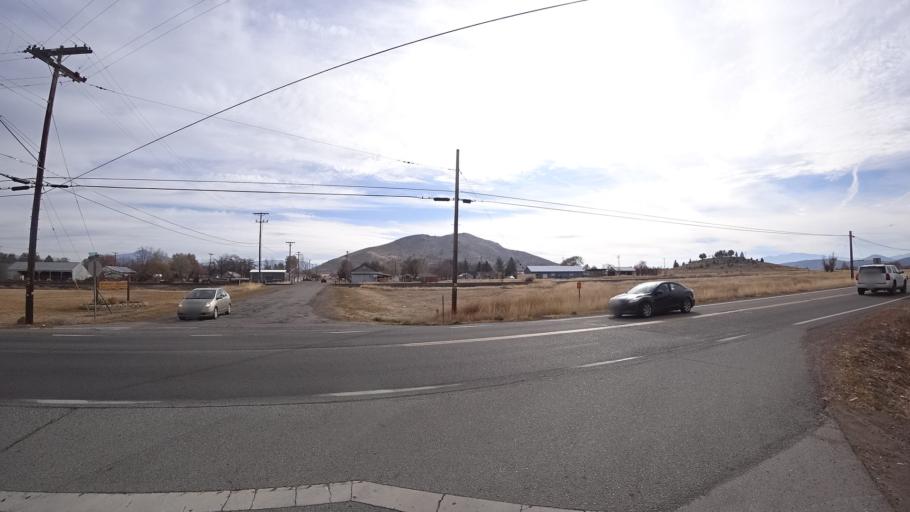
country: US
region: California
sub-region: Siskiyou County
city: Montague
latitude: 41.7258
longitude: -122.5294
